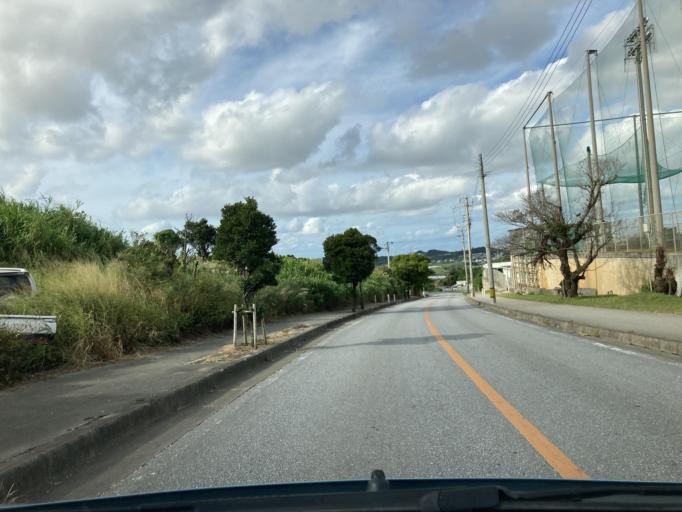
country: JP
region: Okinawa
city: Itoman
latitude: 26.1285
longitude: 127.7106
